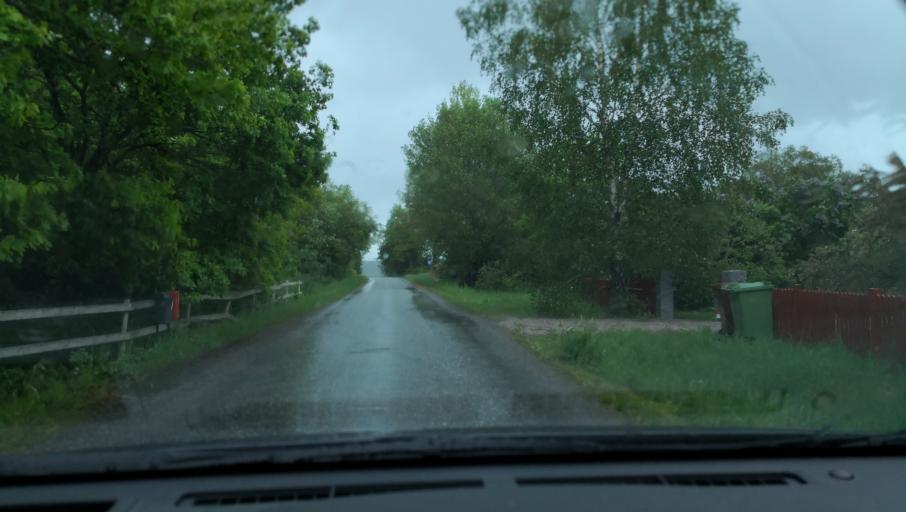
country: SE
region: Uppsala
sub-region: Enkopings Kommun
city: Orsundsbro
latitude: 59.7719
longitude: 17.3447
